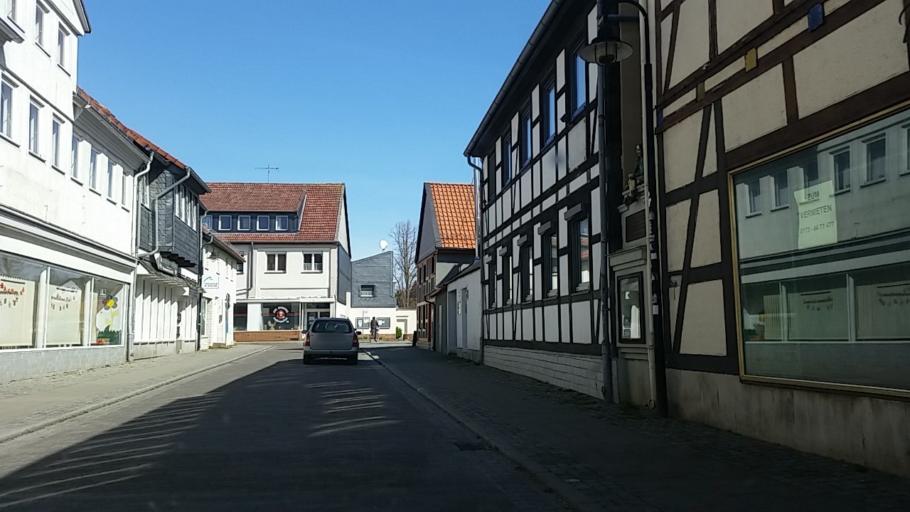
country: DE
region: Lower Saxony
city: Schoppenstedt
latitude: 52.1449
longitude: 10.7748
